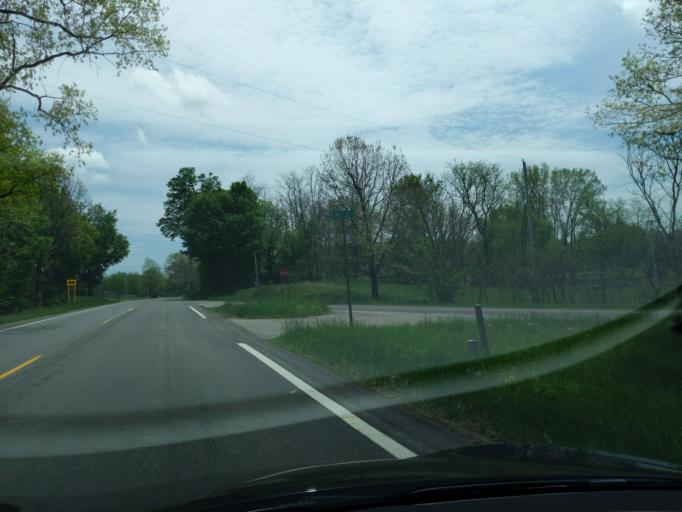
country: US
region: Michigan
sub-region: Ingham County
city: Stockbridge
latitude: 42.5050
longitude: -84.1464
